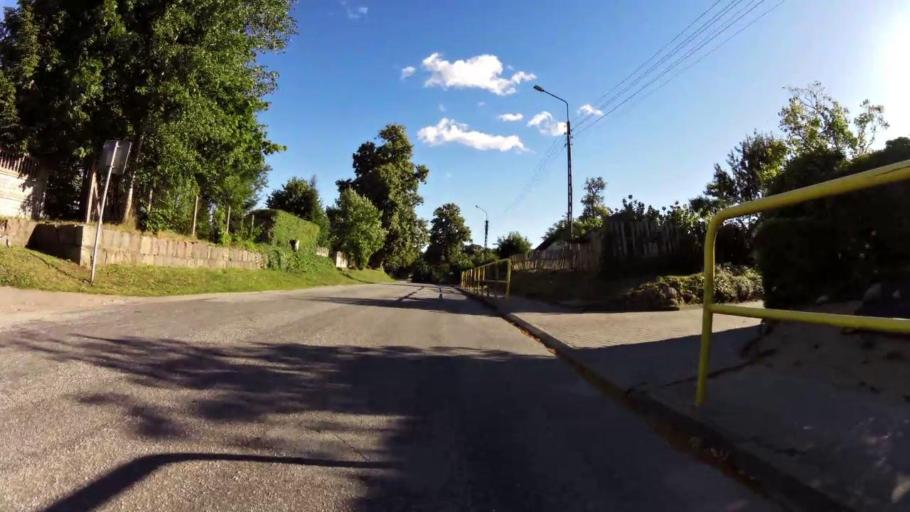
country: PL
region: West Pomeranian Voivodeship
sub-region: Powiat swidwinski
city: Swidwin
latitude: 53.7581
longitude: 15.6933
